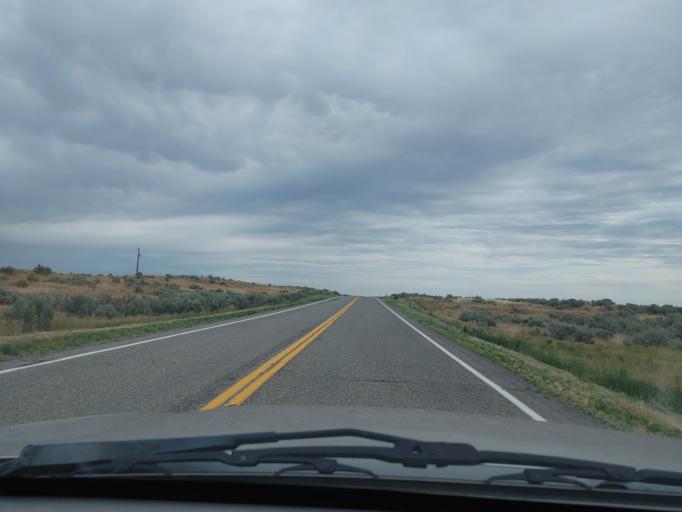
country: US
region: Idaho
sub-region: Lincoln County
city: Shoshone
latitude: 43.0561
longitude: -114.1339
